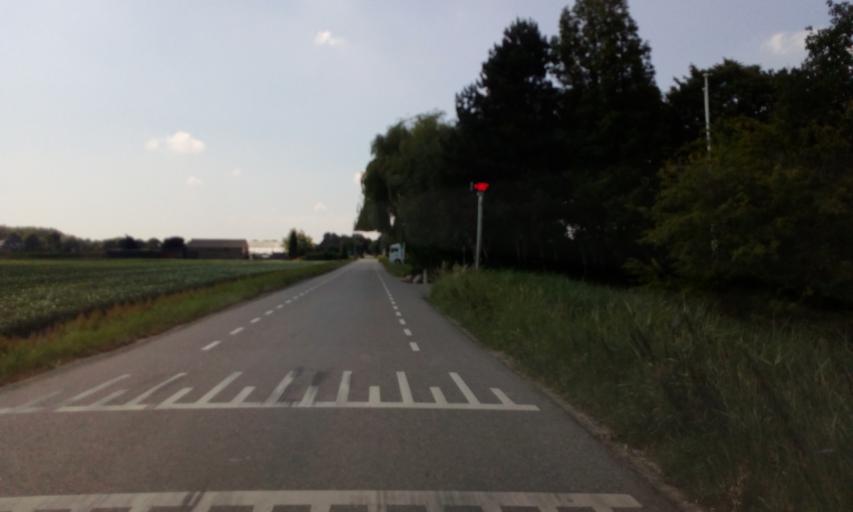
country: NL
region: South Holland
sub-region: Gemeente Rijnwoude
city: Benthuizen
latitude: 52.0830
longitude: 4.5552
